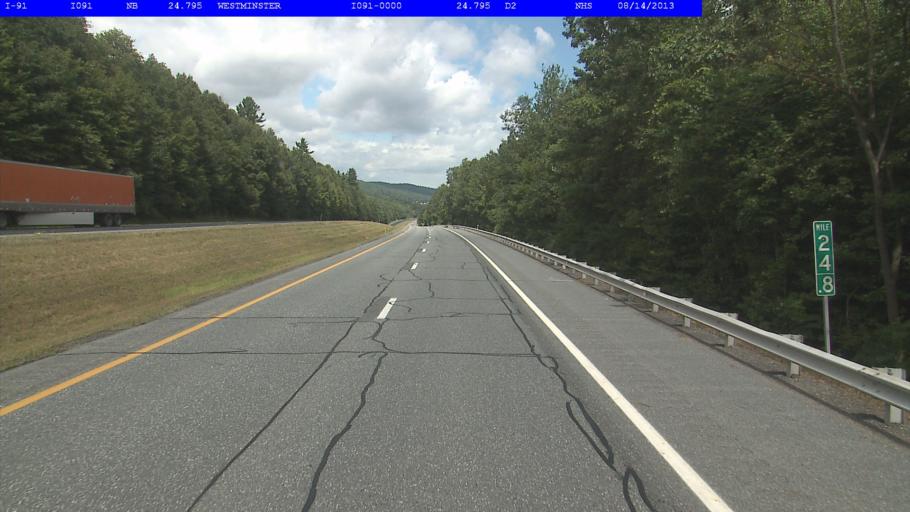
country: US
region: New Hampshire
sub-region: Cheshire County
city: Westmoreland
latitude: 43.0381
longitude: -72.4686
